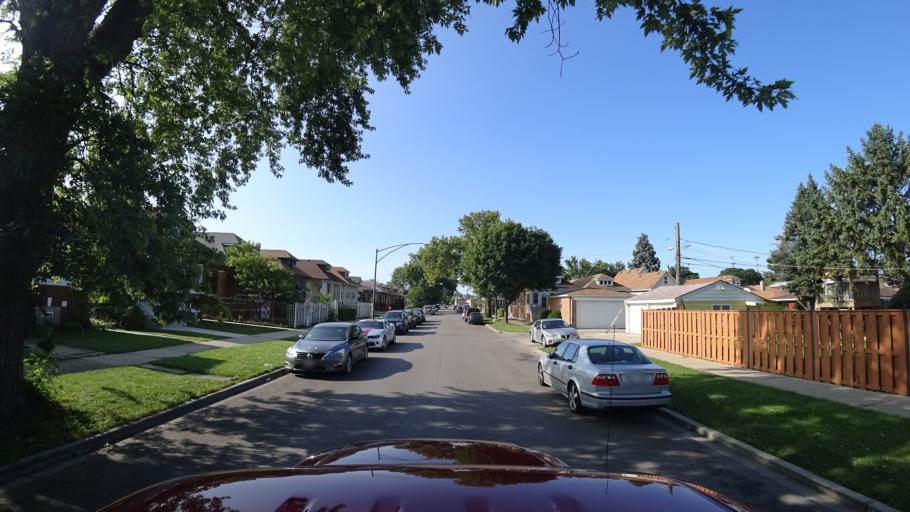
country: US
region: Illinois
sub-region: Cook County
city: Hometown
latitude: 41.7878
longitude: -87.7108
